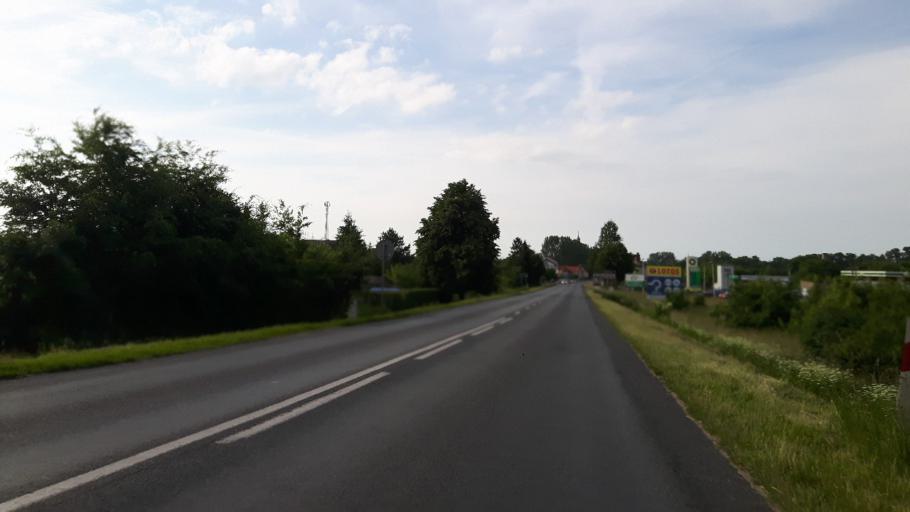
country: PL
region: West Pomeranian Voivodeship
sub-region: Powiat gryficki
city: Gryfice
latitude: 53.9038
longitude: 15.2023
